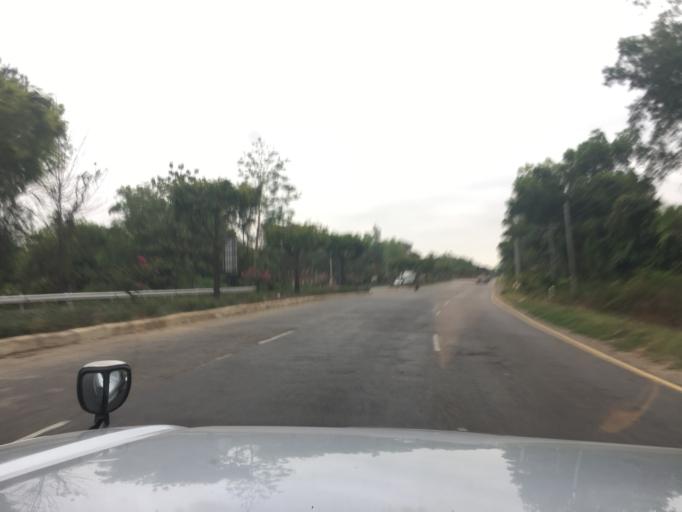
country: MM
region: Bago
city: Bago
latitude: 17.2210
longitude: 96.4372
